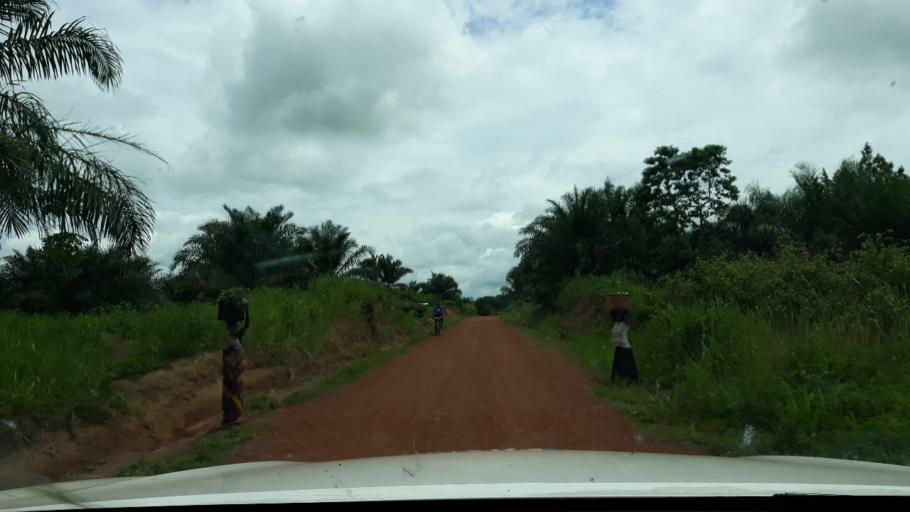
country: CD
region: Equateur
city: Gemena
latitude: 3.5604
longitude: 19.3099
